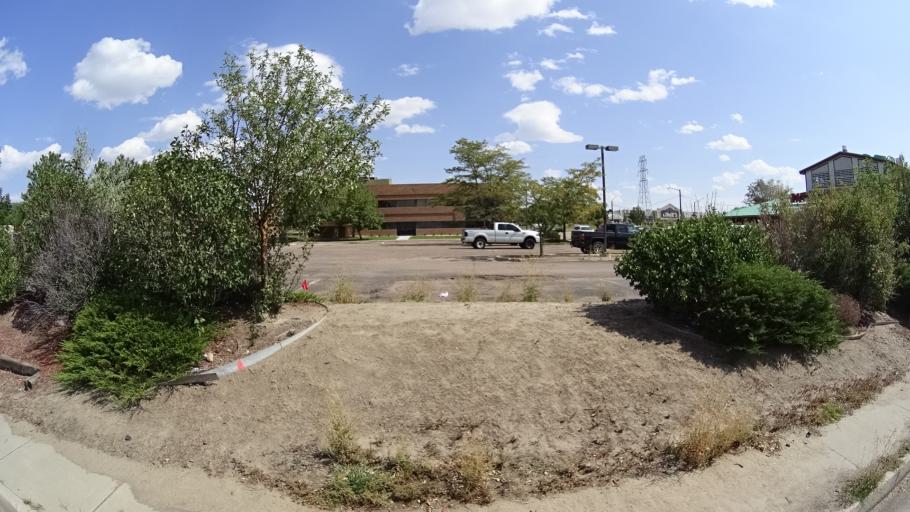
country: US
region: Colorado
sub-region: El Paso County
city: Cimarron Hills
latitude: 38.8448
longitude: -104.7587
